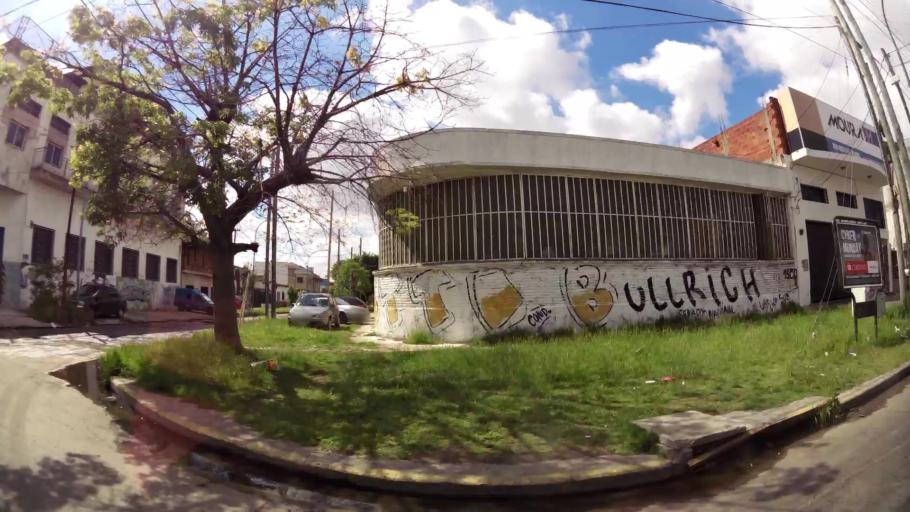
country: AR
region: Buenos Aires
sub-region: Partido de Lanus
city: Lanus
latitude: -34.6835
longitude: -58.4075
